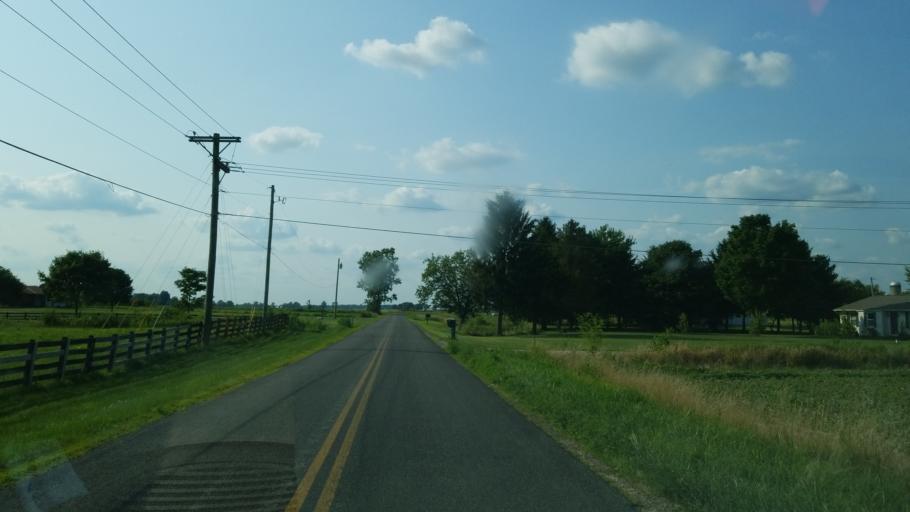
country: US
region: Ohio
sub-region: Union County
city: New California
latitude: 40.1787
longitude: -83.2801
